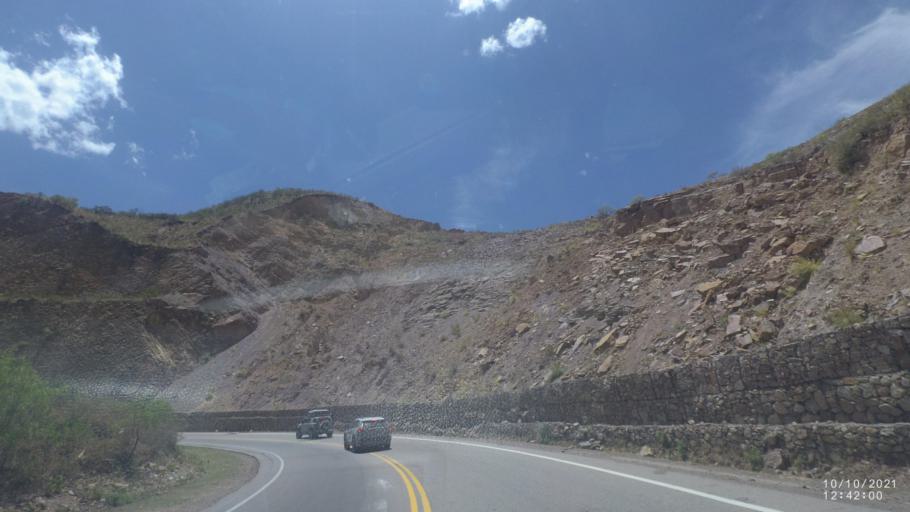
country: BO
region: Cochabamba
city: Irpa Irpa
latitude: -17.6311
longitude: -66.3897
